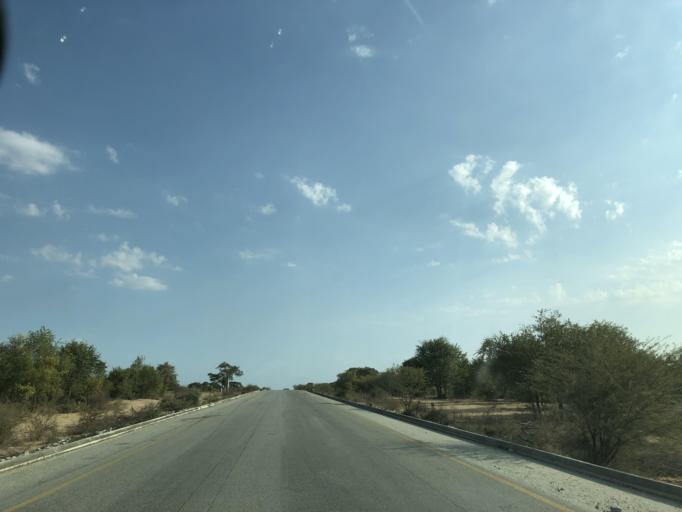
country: AO
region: Benguela
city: Benguela
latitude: -13.2050
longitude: 13.7636
